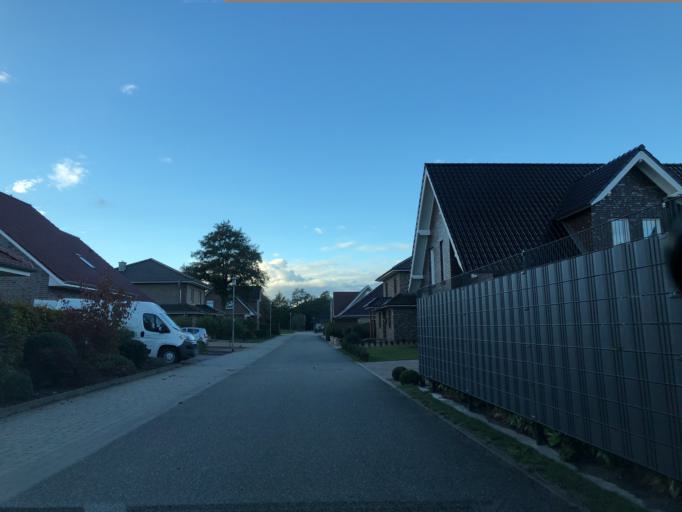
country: DE
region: Lower Saxony
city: Papenburg
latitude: 53.0861
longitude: 7.4110
